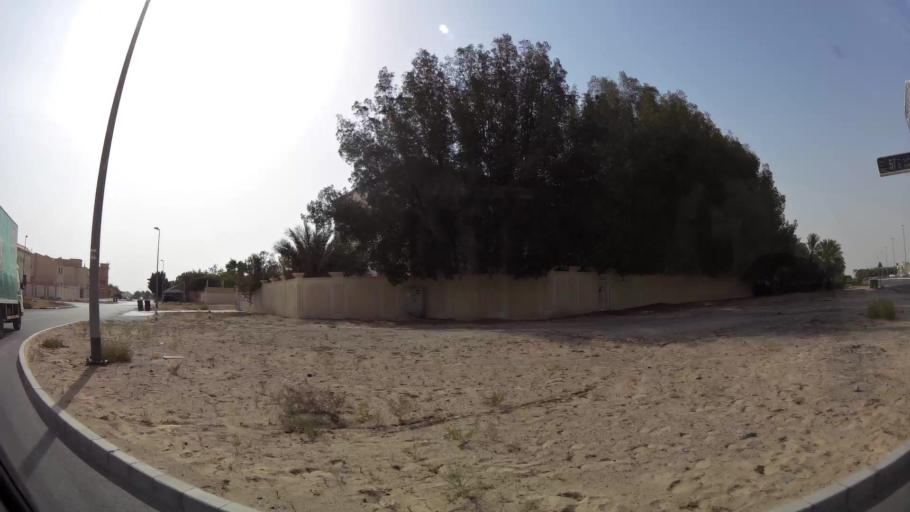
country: AE
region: Ash Shariqah
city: Sharjah
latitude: 25.2547
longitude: 55.4552
